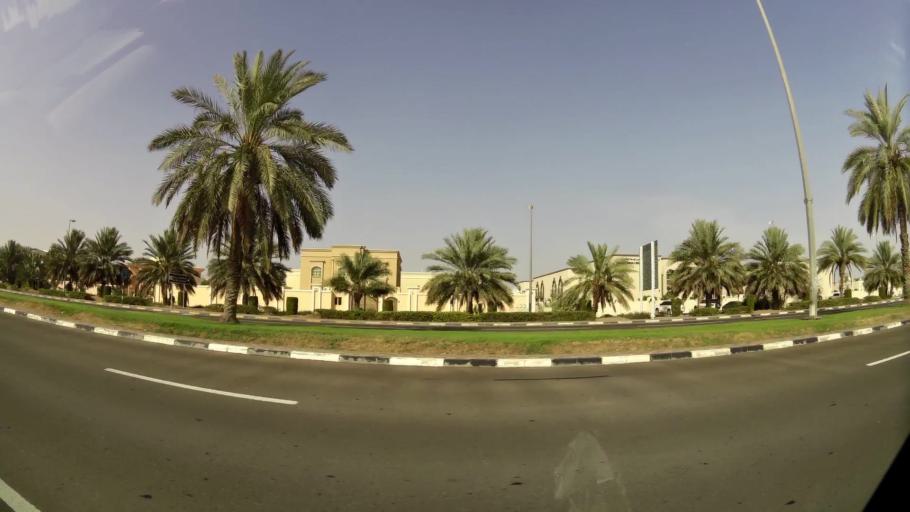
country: AE
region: Abu Dhabi
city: Al Ain
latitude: 24.2310
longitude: 55.6800
